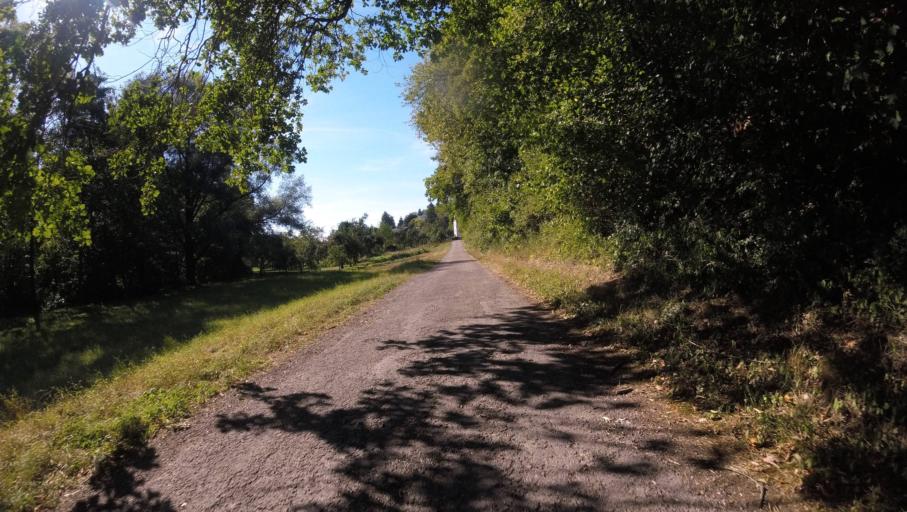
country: DE
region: Baden-Wuerttemberg
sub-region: Regierungsbezirk Stuttgart
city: Kirchberg an der Murr
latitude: 48.9403
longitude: 9.3352
